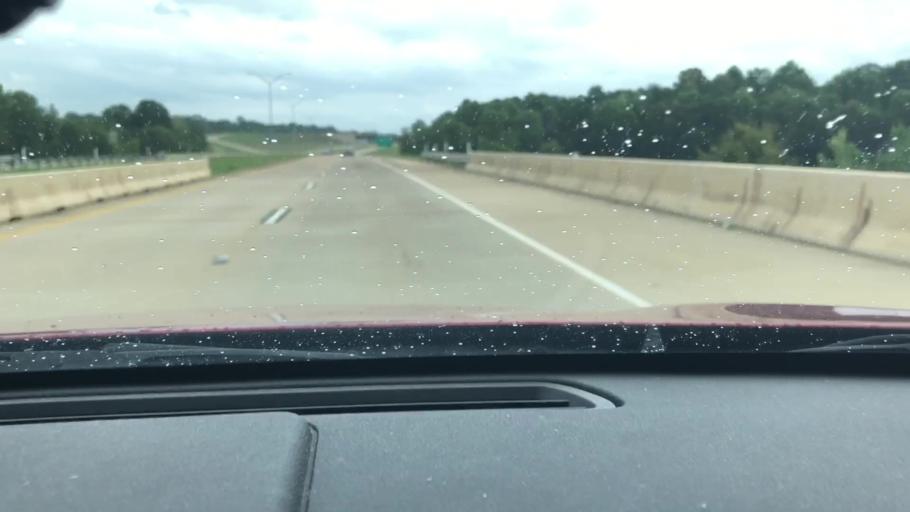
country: US
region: Texas
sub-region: Bowie County
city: Texarkana
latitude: 33.3848
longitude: -94.0510
